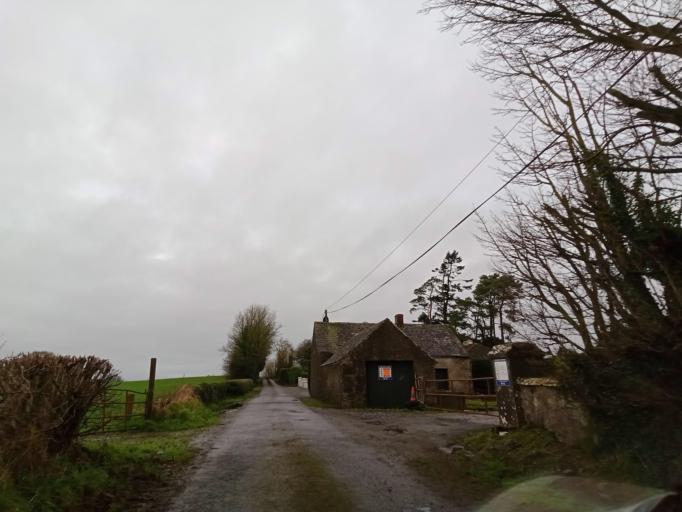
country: IE
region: Munster
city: Fethard
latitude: 52.5598
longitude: -7.7098
